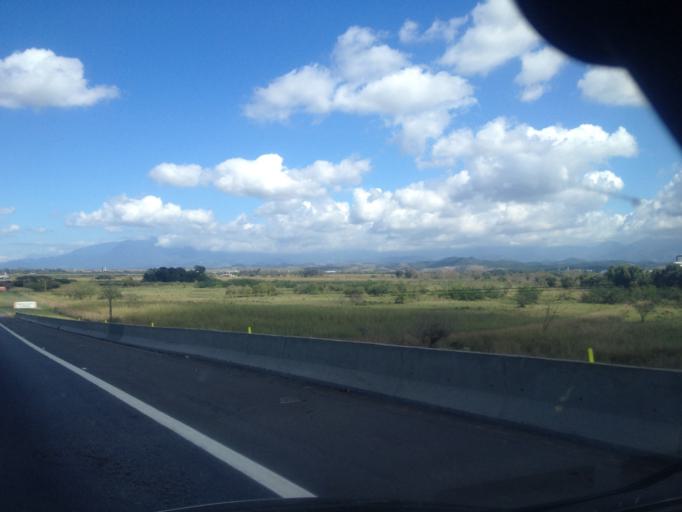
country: BR
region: Rio de Janeiro
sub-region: Porto Real
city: Porto Real
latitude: -22.4501
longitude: -44.3314
